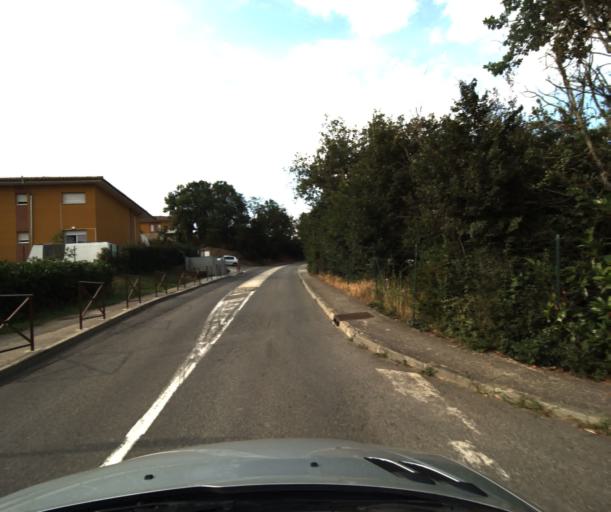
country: FR
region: Midi-Pyrenees
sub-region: Departement de la Haute-Garonne
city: Fonsorbes
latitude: 43.5305
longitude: 1.2310
